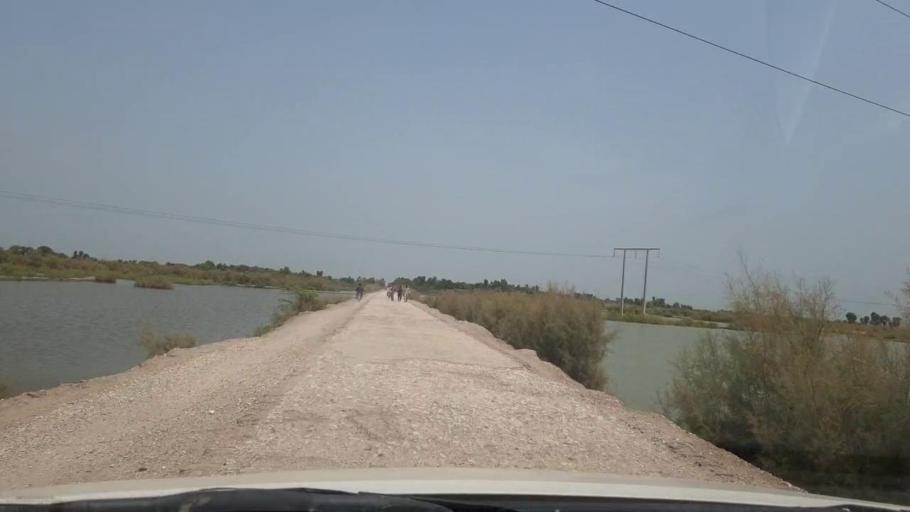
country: PK
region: Sindh
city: Rustam jo Goth
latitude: 28.0267
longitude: 68.8130
